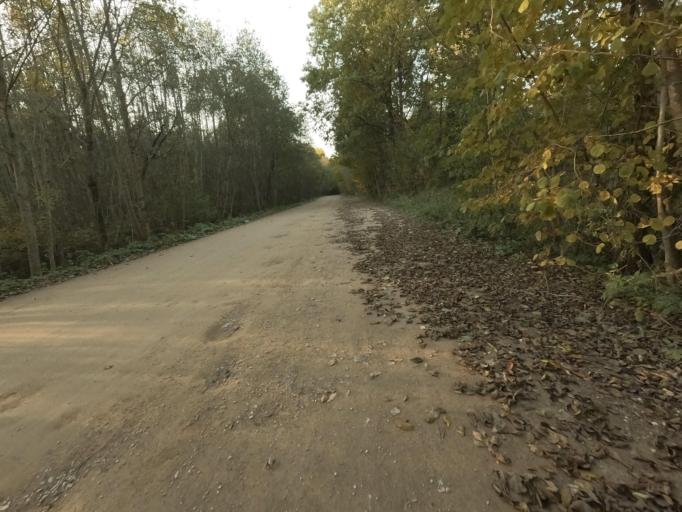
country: RU
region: Leningrad
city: Lyuban'
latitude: 59.0029
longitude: 31.0978
